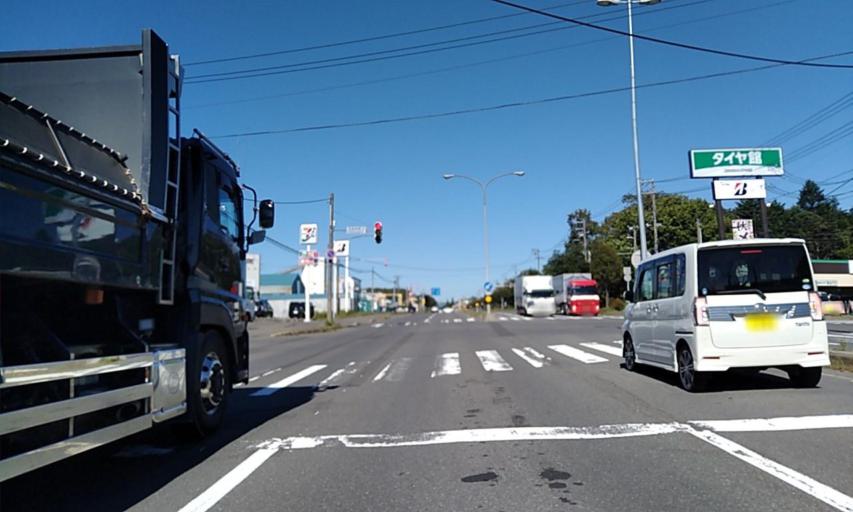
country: JP
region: Hokkaido
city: Kitahiroshima
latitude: 42.9016
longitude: 141.5580
